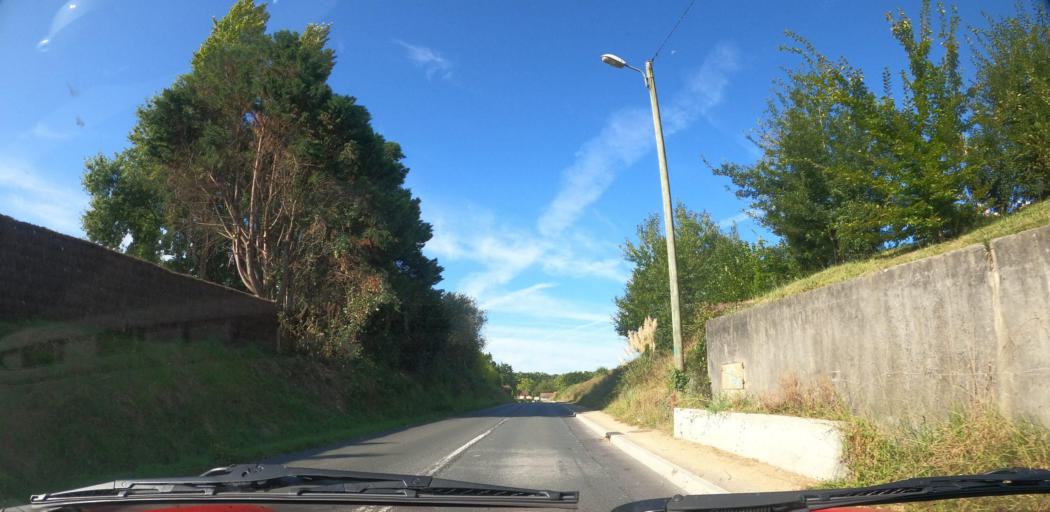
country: FR
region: Aquitaine
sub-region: Departement des Pyrenees-Atlantiques
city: Arbonne
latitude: 43.4394
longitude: -1.5477
